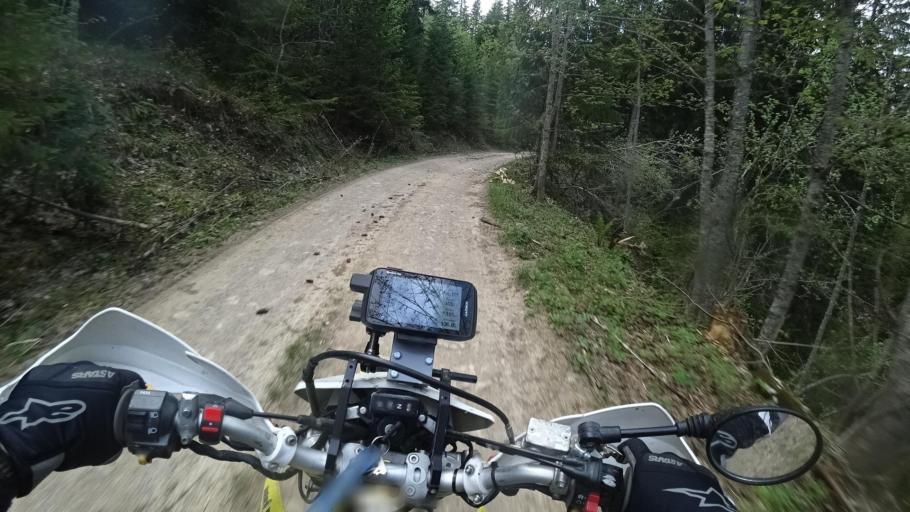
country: BA
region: Republika Srpska
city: Sipovo
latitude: 44.1169
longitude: 17.0798
